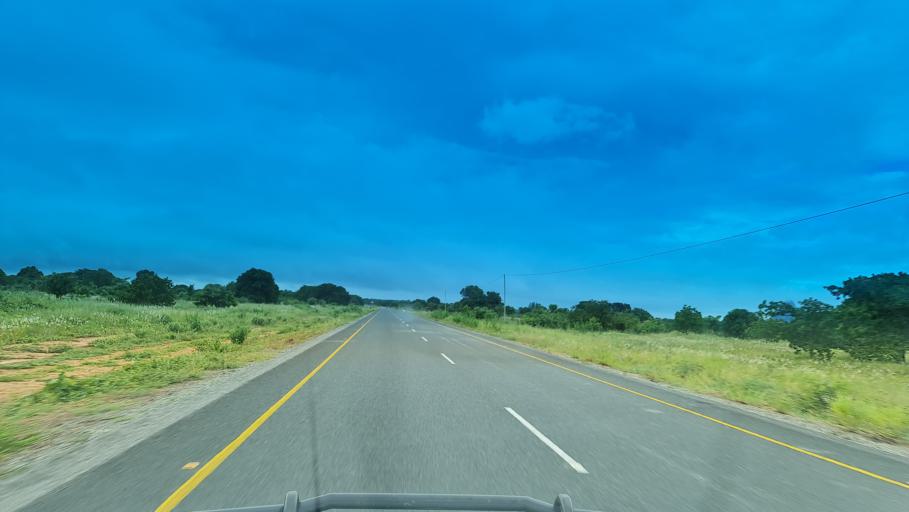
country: MZ
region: Nampula
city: Nampula
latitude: -15.5750
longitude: 39.3233
